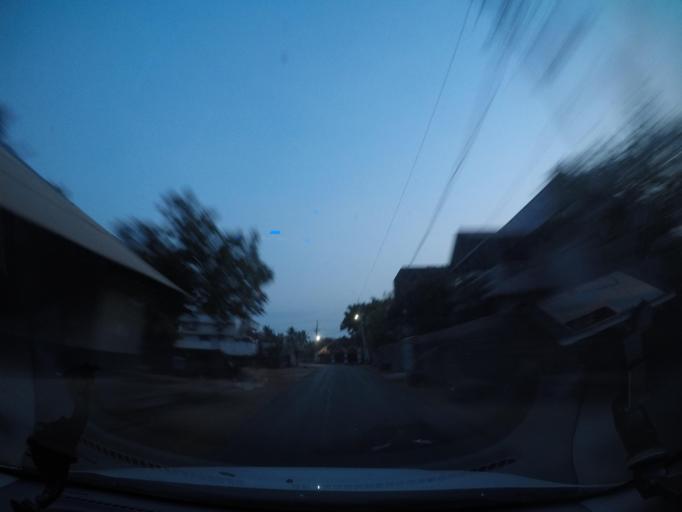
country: IN
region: Andhra Pradesh
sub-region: West Godavari
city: Tadepallegudem
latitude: 16.7816
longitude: 81.4249
